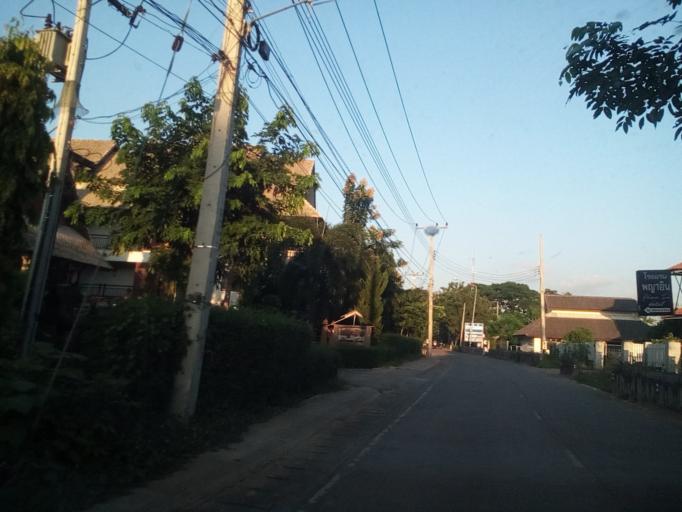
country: TH
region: Lamphun
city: Lamphun
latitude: 18.5827
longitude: 99.0155
